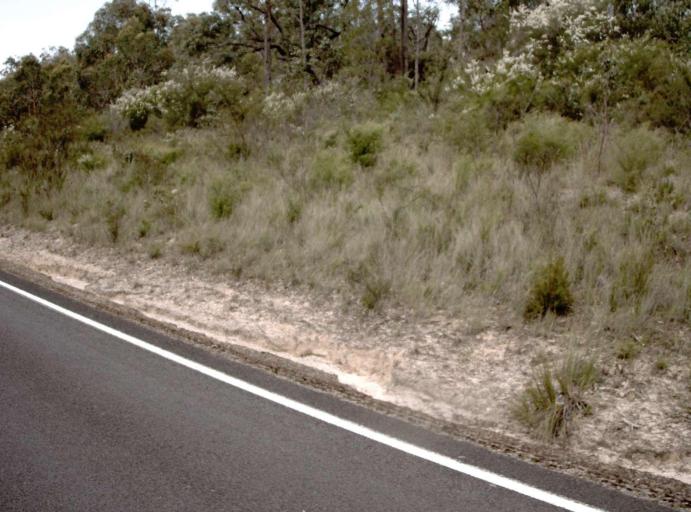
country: AU
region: New South Wales
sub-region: Bega Valley
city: Eden
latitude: -37.4844
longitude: 149.5510
